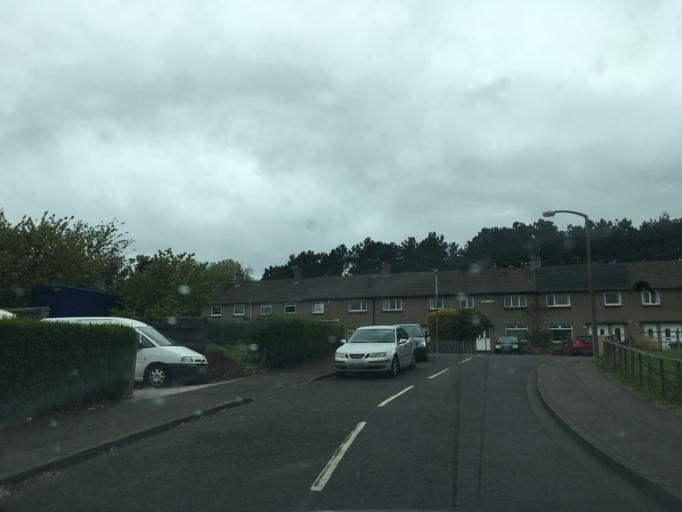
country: GB
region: Scotland
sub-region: Edinburgh
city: Colinton
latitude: 55.9127
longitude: -3.2259
